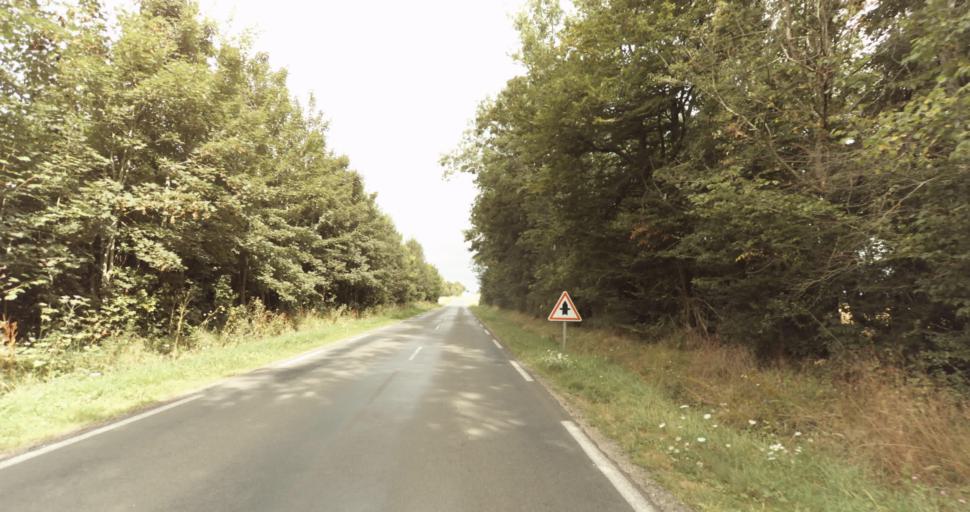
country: FR
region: Haute-Normandie
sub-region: Departement de l'Eure
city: Gravigny
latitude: 49.0186
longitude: 1.2437
